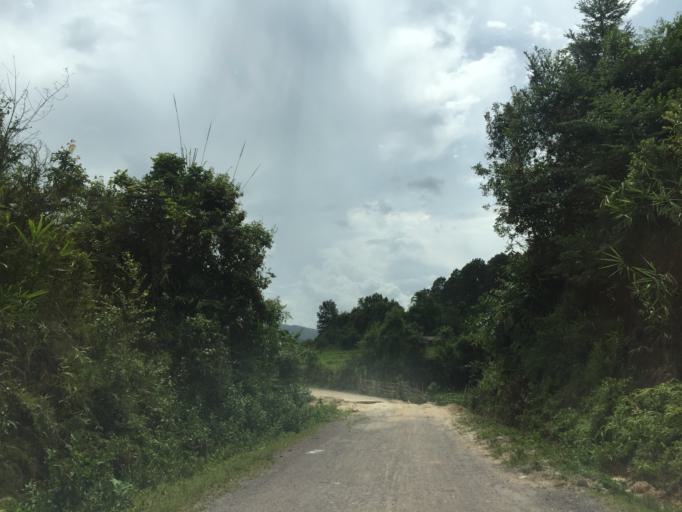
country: LA
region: Xiangkhoang
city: Muang Phonsavan
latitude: 19.3418
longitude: 103.5514
